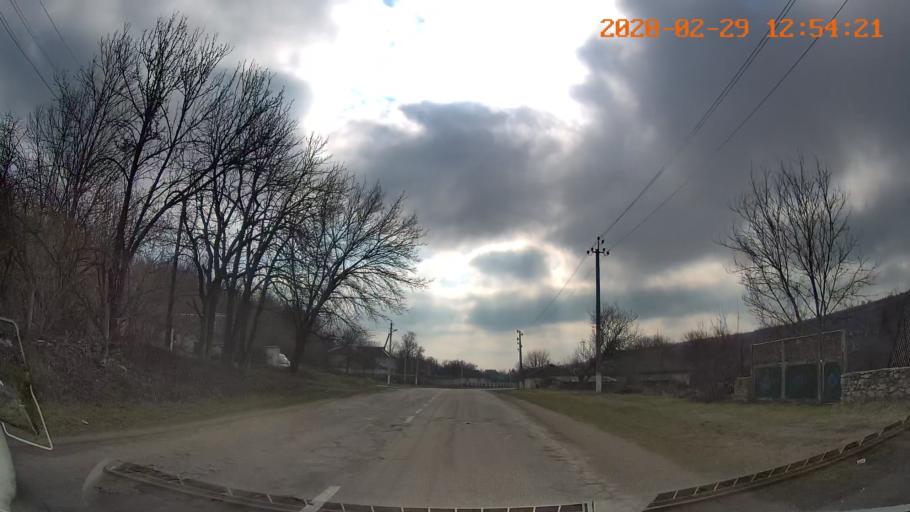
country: MD
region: Telenesti
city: Camenca
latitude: 48.1025
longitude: 28.7278
